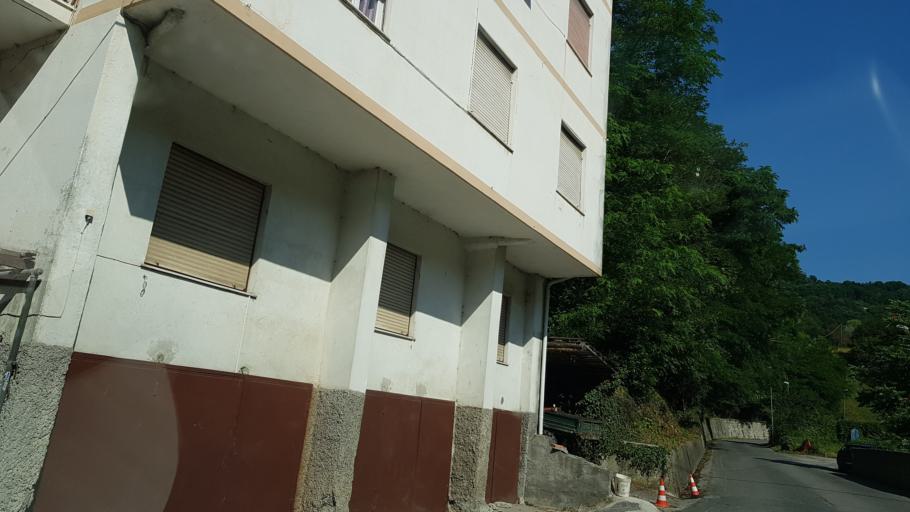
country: IT
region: Liguria
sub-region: Provincia di Genova
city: Serra Ricco
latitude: 44.5140
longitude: 8.9402
